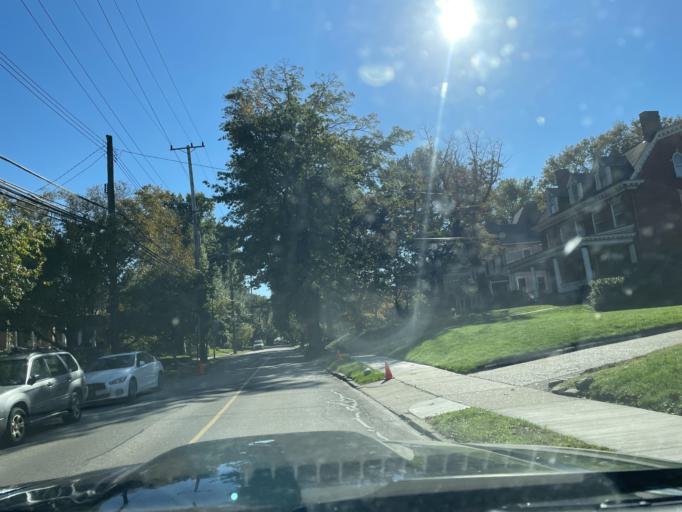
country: US
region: Pennsylvania
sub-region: Allegheny County
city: Edgewood
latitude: 40.4323
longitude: -79.8823
